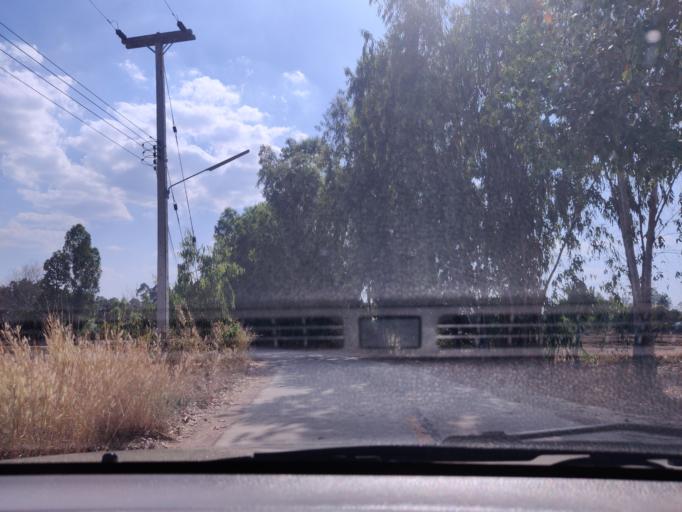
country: TH
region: Sisaket
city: Si Sa Ket
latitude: 15.0825
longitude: 104.3513
